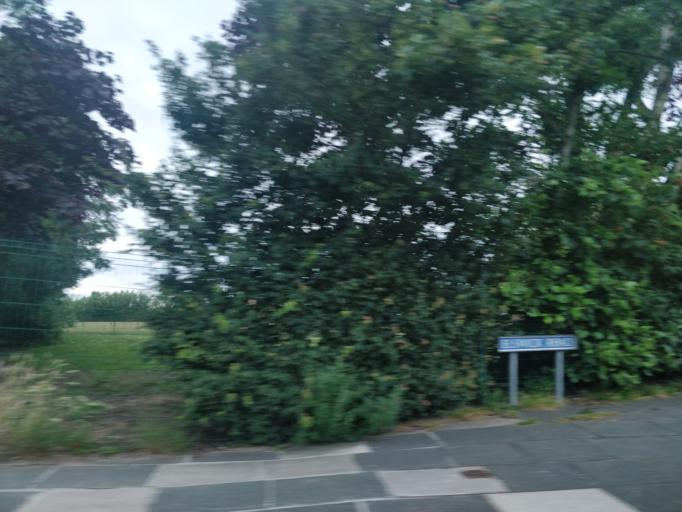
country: GB
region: England
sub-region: Sefton
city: Southport
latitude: 53.6731
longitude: -2.9701
